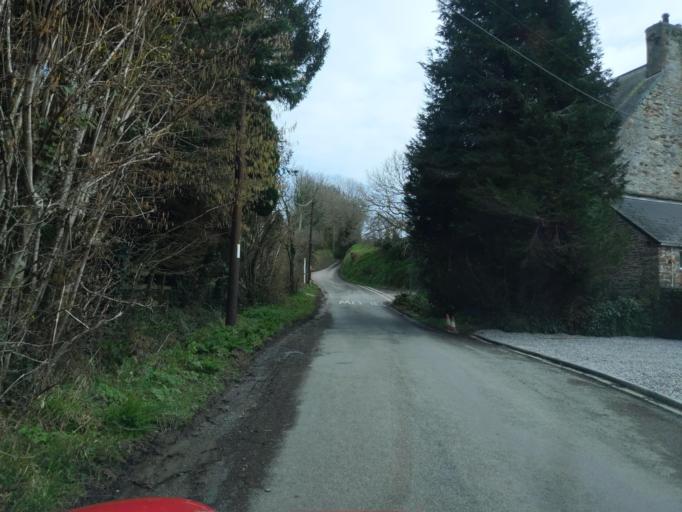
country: GB
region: England
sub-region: Devon
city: Yealmpton
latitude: 50.3642
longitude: -4.0117
